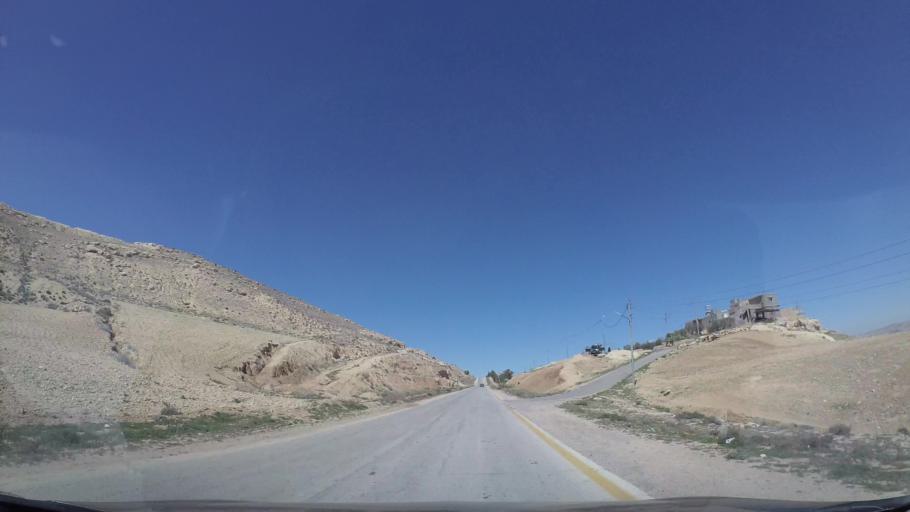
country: JO
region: Tafielah
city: At Tafilah
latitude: 30.8435
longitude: 35.5614
